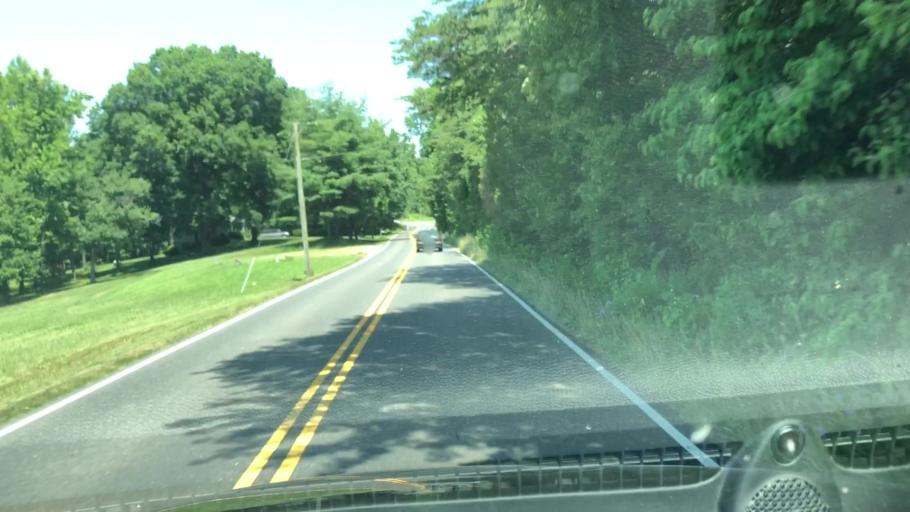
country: US
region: Virginia
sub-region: Stafford County
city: Falmouth
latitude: 38.4219
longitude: -77.5732
